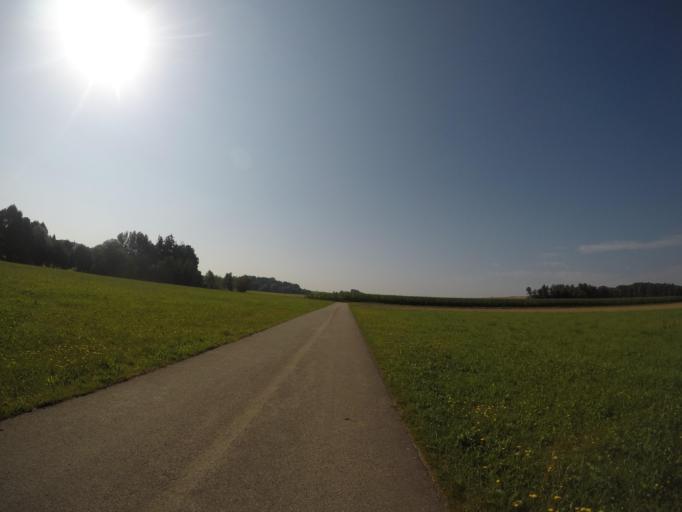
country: DE
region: Baden-Wuerttemberg
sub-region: Tuebingen Region
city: Wain
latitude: 48.2101
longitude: 10.0153
